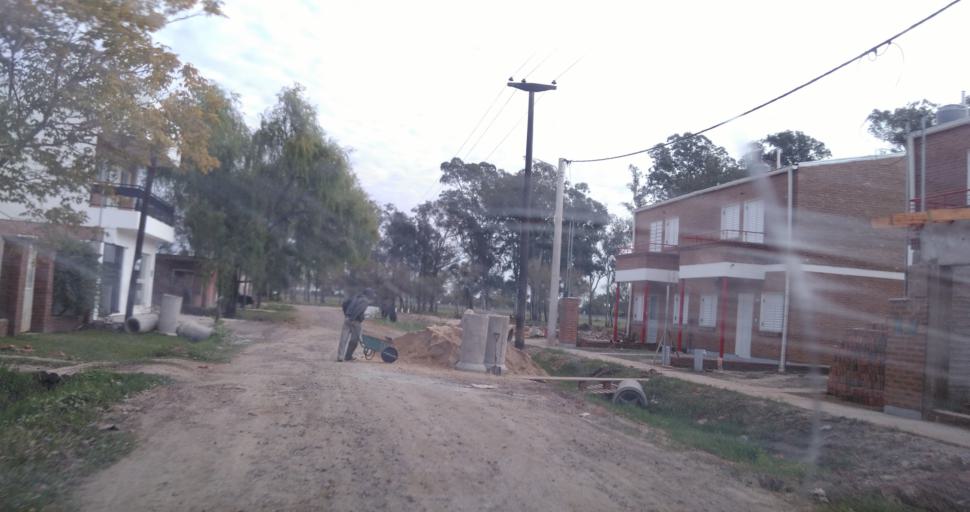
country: AR
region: Chaco
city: Fontana
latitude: -27.4429
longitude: -59.0300
